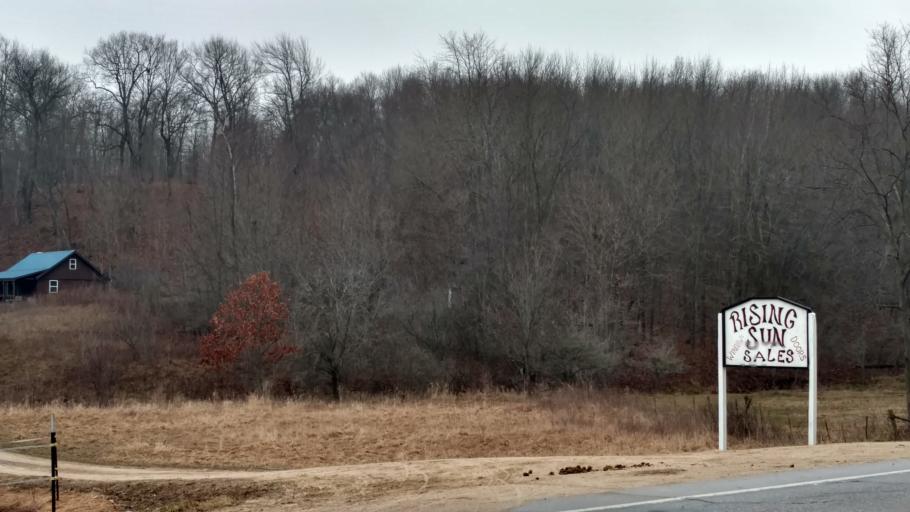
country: US
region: Wisconsin
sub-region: Vernon County
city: Hillsboro
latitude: 43.6407
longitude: -90.4429
